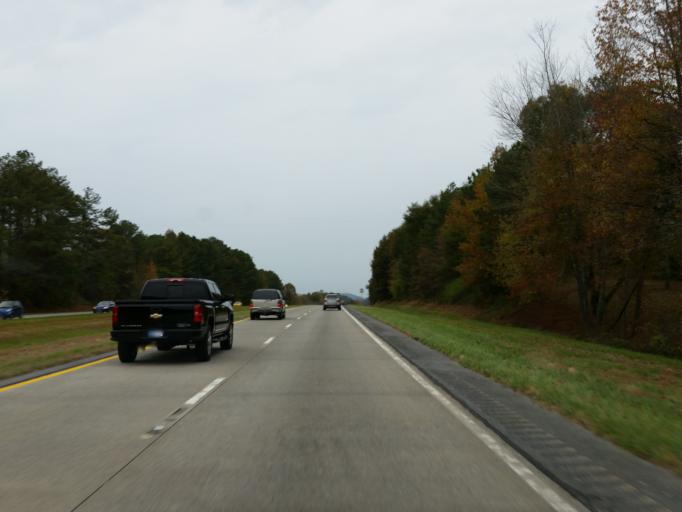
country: US
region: Georgia
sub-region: Pickens County
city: Nelson
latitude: 34.3875
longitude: -84.4012
